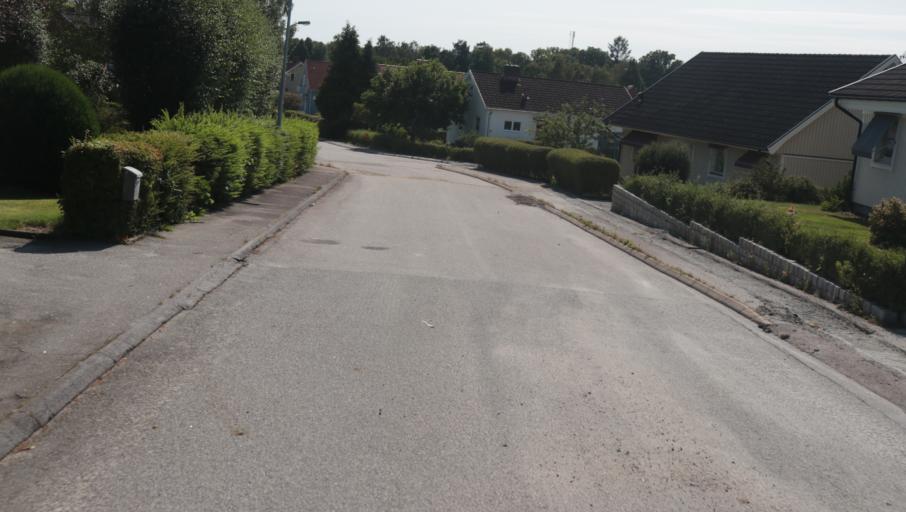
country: SE
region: Blekinge
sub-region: Karlshamns Kommun
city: Karlshamn
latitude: 56.2114
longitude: 14.8322
